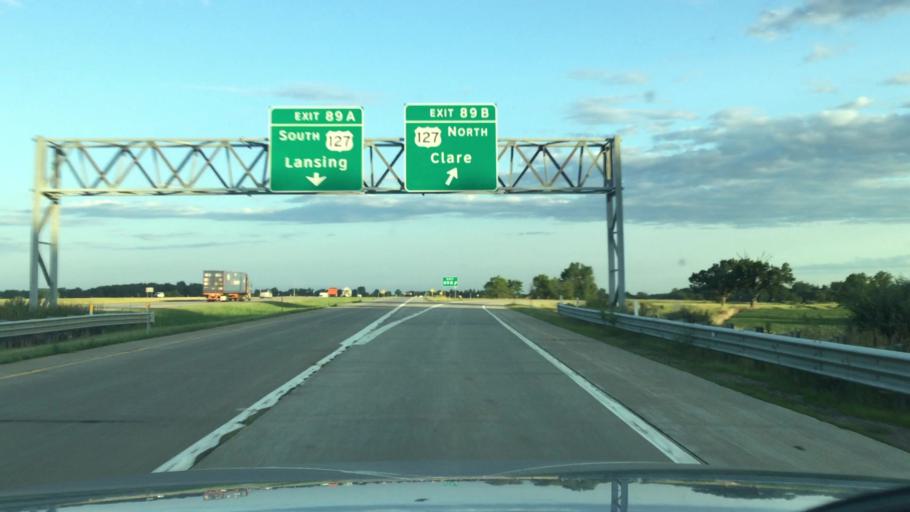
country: US
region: Michigan
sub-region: Clinton County
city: Bath
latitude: 42.8040
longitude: -84.5043
